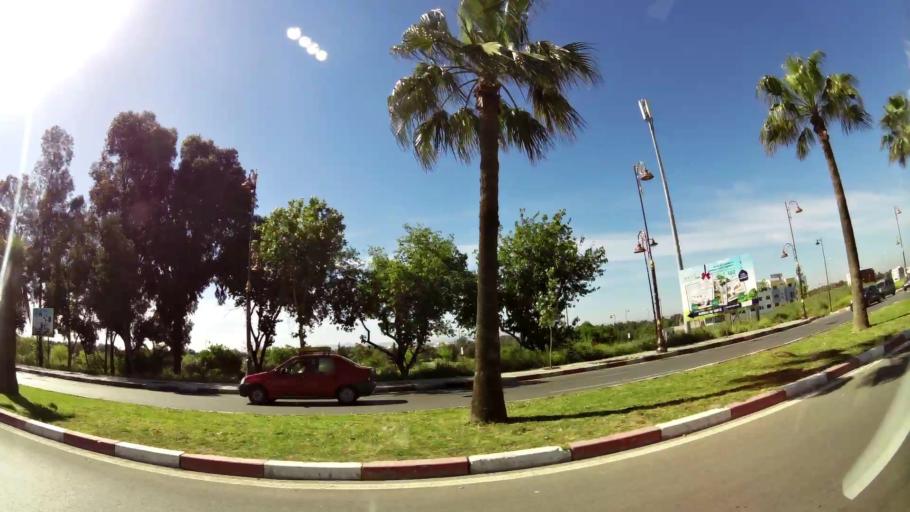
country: MA
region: Fes-Boulemane
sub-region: Fes
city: Fes
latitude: 34.0558
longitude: -5.0190
